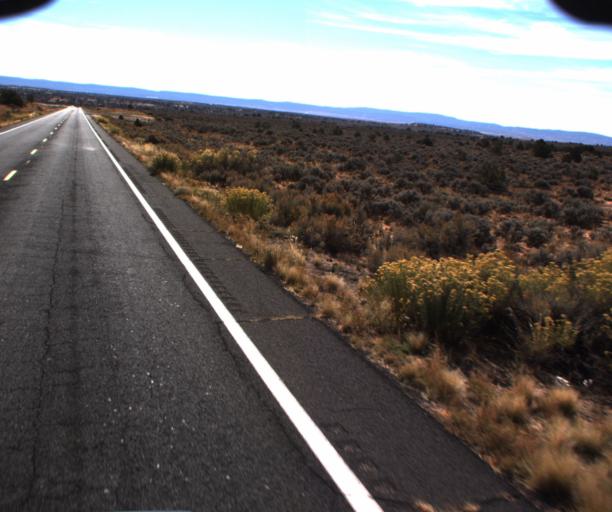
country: US
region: Arizona
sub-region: Coconino County
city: Kaibito
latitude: 36.5644
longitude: -110.7562
